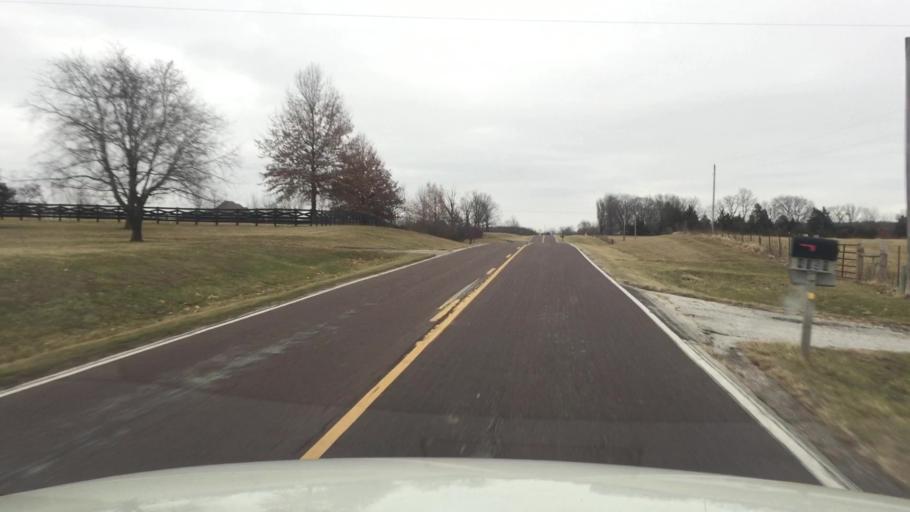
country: US
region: Missouri
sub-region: Boone County
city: Ashland
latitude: 38.8689
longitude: -92.2799
